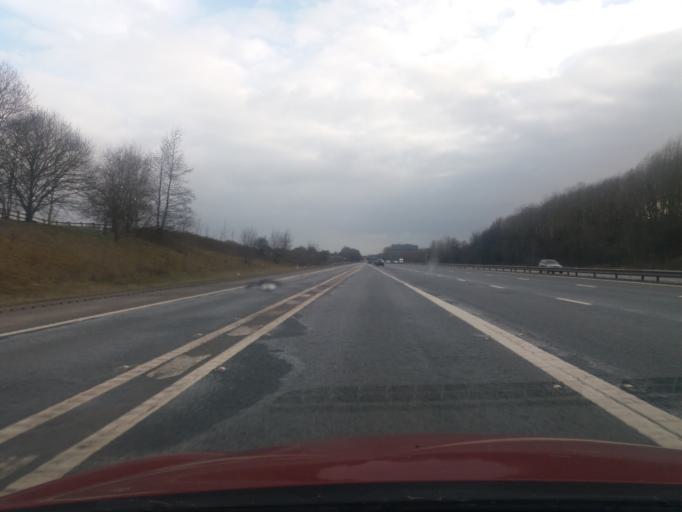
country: GB
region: England
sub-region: Lancashire
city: Clayton-le-Woods
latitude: 53.7139
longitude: -2.6303
